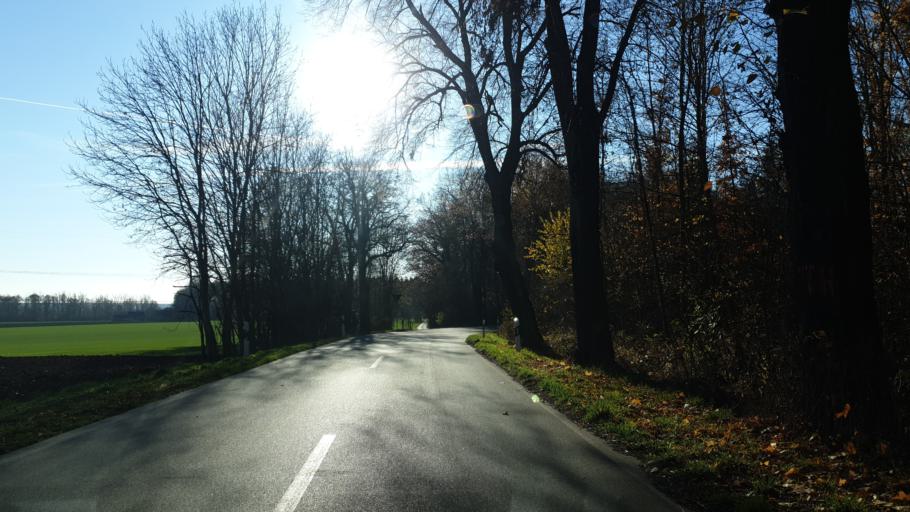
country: DE
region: Saxony-Anhalt
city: Droyssig
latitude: 51.0283
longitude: 12.0209
